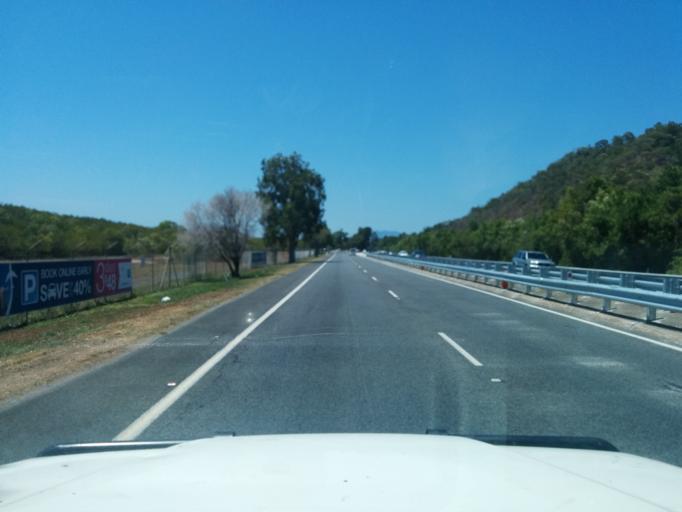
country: AU
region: Queensland
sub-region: Cairns
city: Cairns
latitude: -16.8891
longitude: 145.7514
